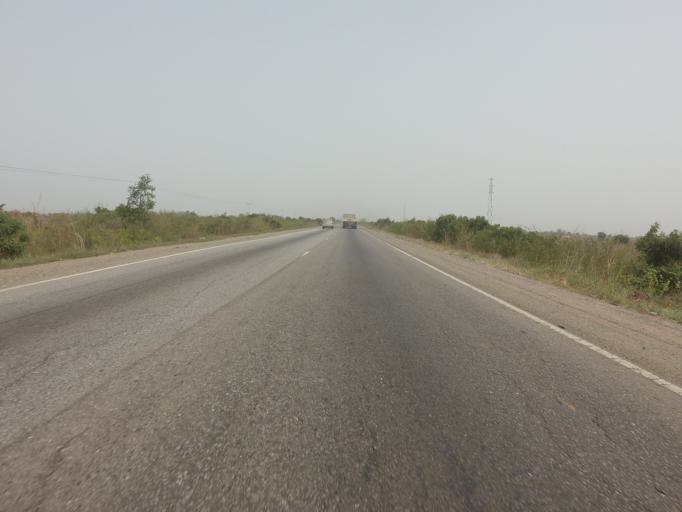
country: GH
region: Greater Accra
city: Tema
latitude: 5.7806
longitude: 0.0928
